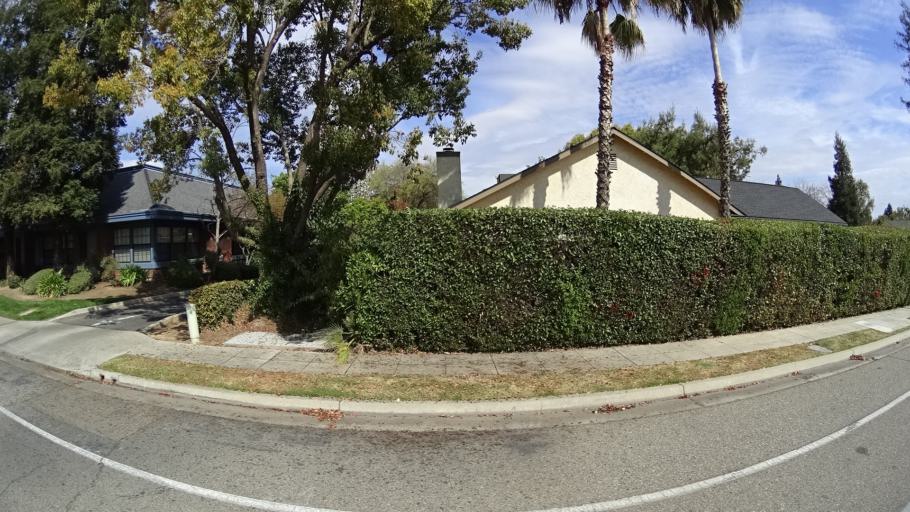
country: US
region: California
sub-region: Fresno County
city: Fresno
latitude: 36.8157
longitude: -119.8065
